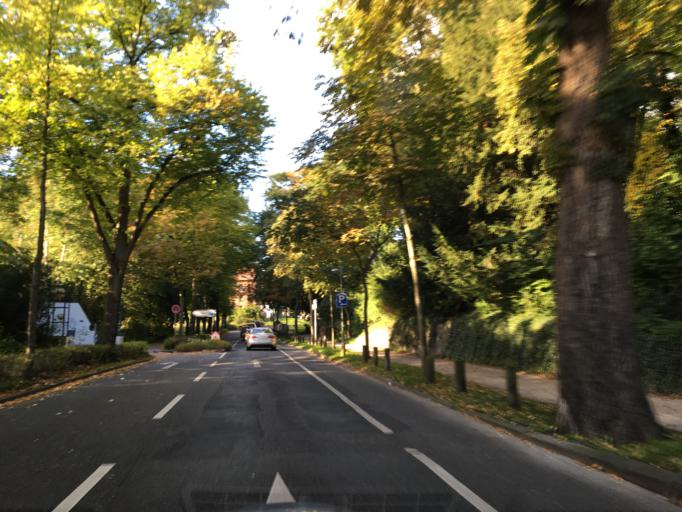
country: DE
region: Lower Saxony
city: Lueneburg
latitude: 53.2511
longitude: 10.4031
